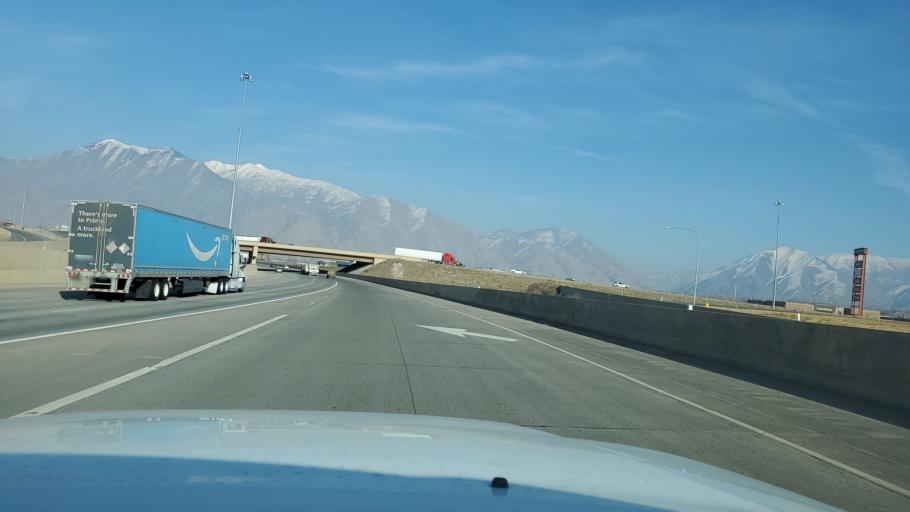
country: US
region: Utah
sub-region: Utah County
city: Spanish Fork
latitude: 40.1263
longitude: -111.6512
